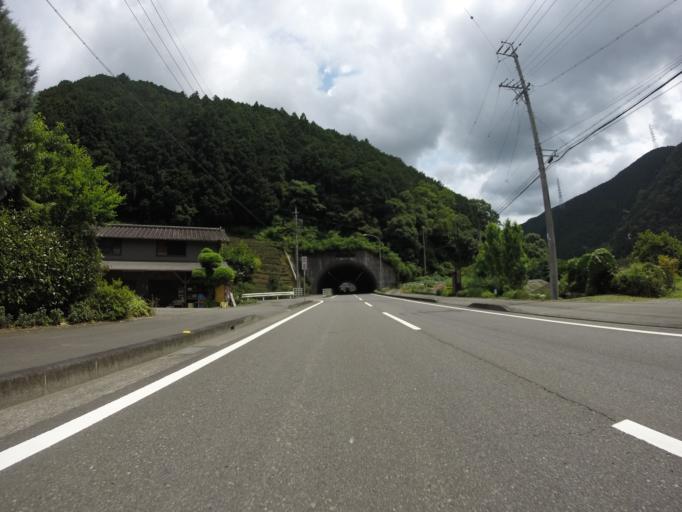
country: JP
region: Shizuoka
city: Shizuoka-shi
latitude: 35.0026
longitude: 138.2867
